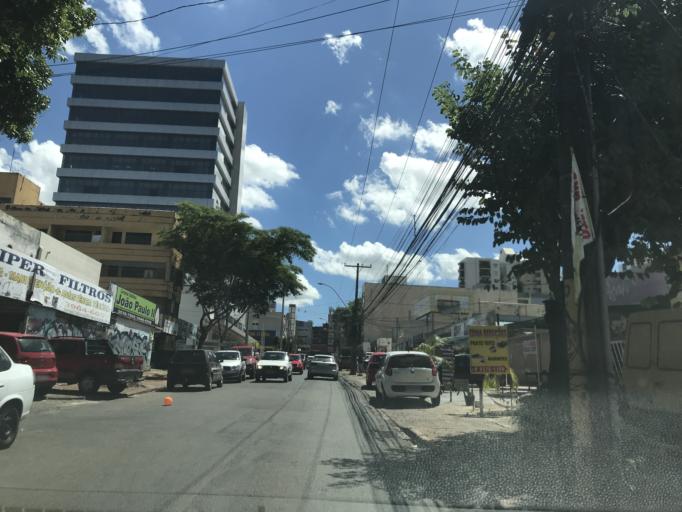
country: BR
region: Federal District
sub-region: Brasilia
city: Brasilia
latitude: -15.8356
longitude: -48.0591
